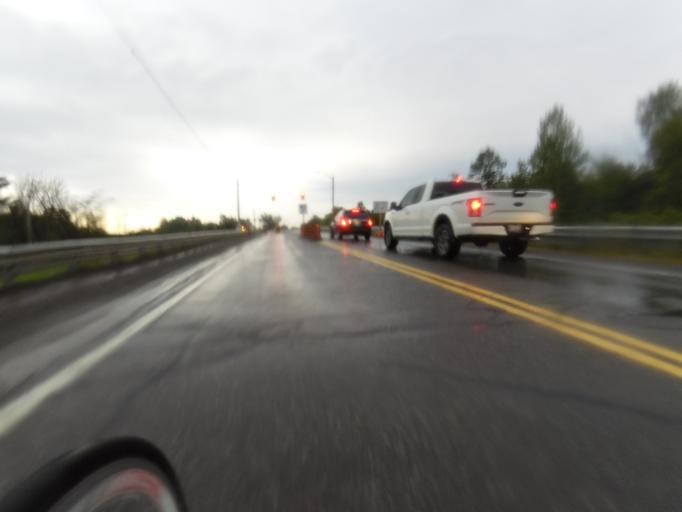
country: CA
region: Ontario
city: Bells Corners
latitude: 45.1955
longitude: -75.7237
